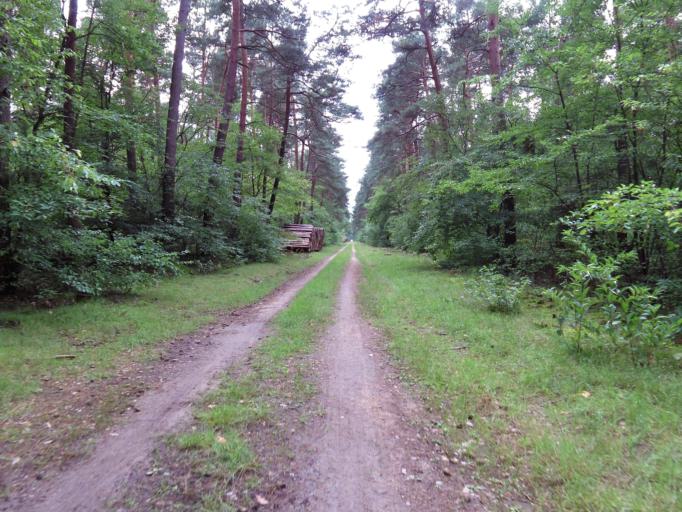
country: DE
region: Hesse
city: Lampertheim
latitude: 49.6159
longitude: 8.5149
